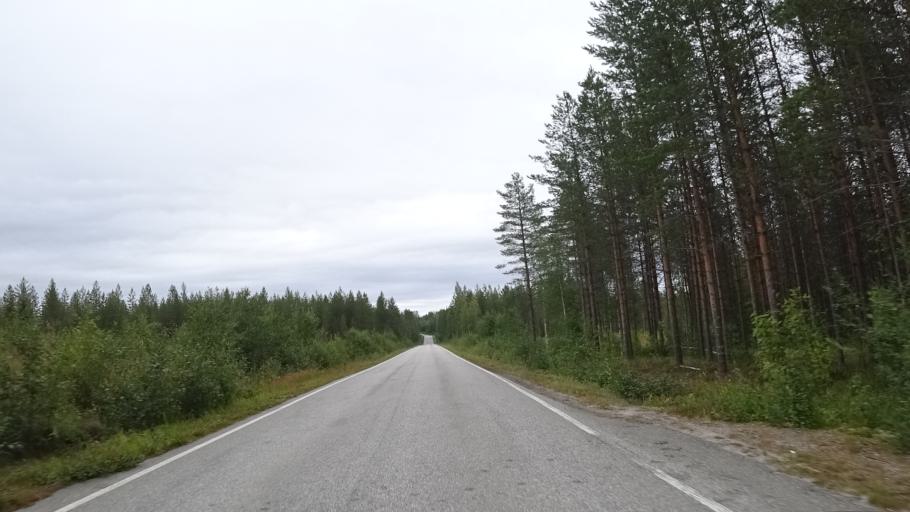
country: FI
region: North Karelia
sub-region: Pielisen Karjala
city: Lieksa
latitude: 63.3704
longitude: 30.2963
